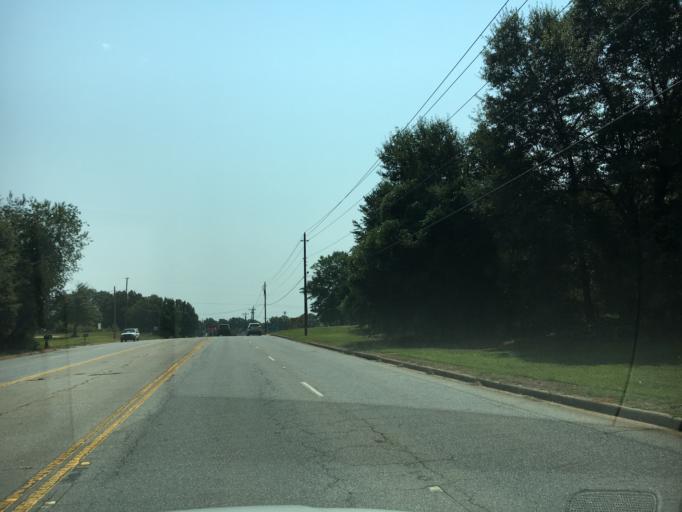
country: US
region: South Carolina
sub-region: Spartanburg County
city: Valley Falls
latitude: 35.0100
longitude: -81.9553
